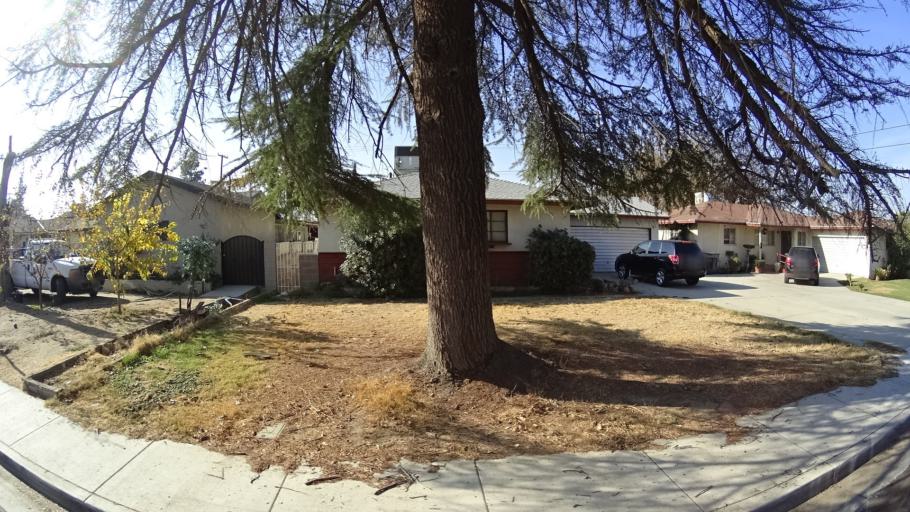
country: US
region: California
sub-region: Kern County
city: Bakersfield
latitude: 35.3277
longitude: -119.0203
